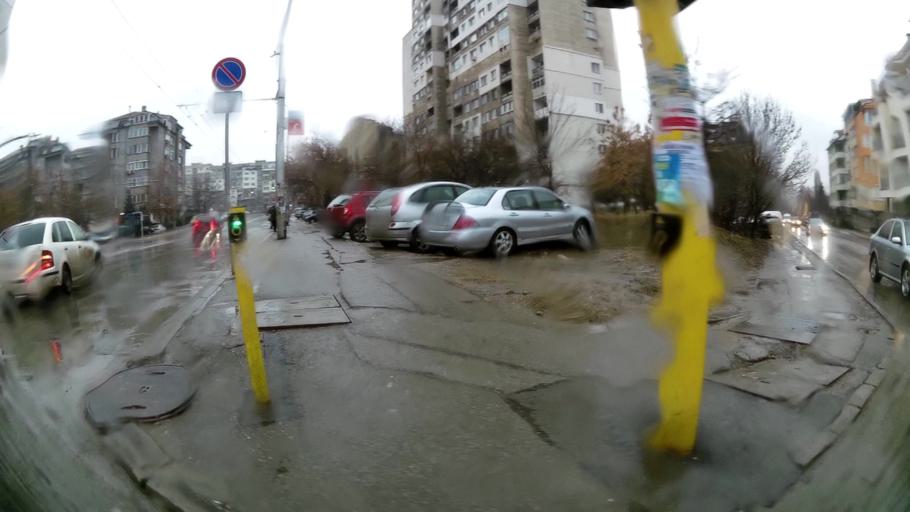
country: BG
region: Sofia-Capital
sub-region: Stolichna Obshtina
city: Sofia
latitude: 42.6570
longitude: 23.3765
